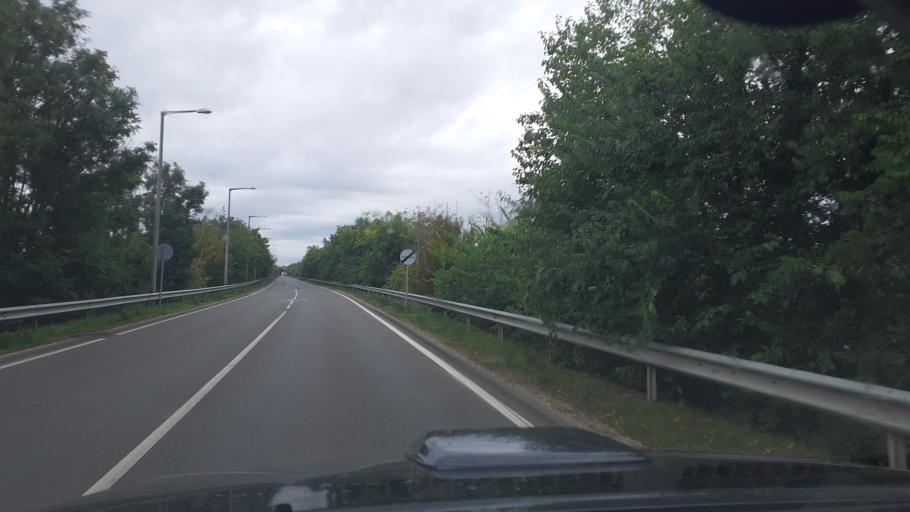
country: HU
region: Tolna
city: Dunafoldvar
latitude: 46.8026
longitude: 18.9277
